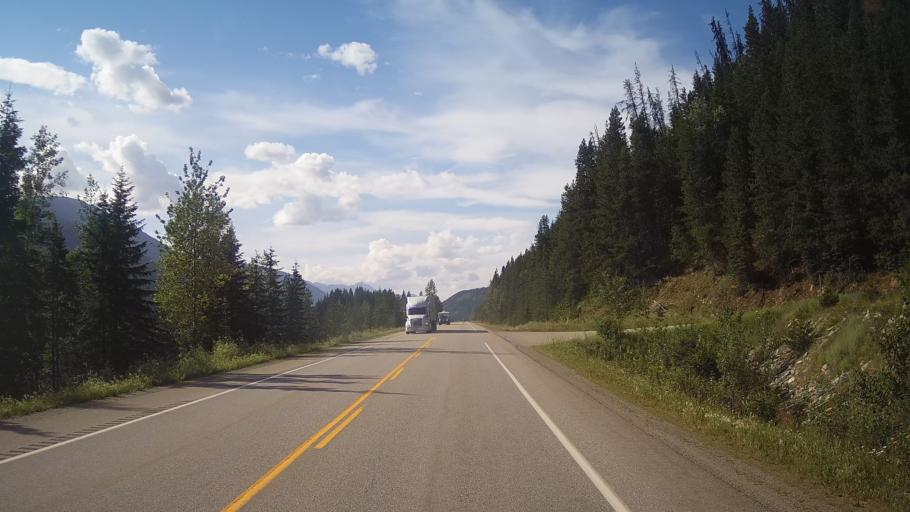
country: CA
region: Alberta
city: Jasper Park Lodge
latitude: 52.6266
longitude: -119.1463
